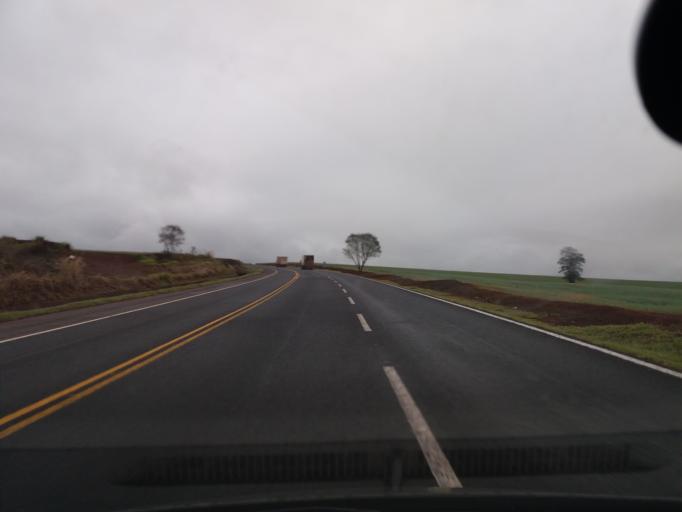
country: BR
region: Parana
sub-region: Campo Mourao
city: Campo Mourao
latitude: -23.9850
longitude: -52.3413
